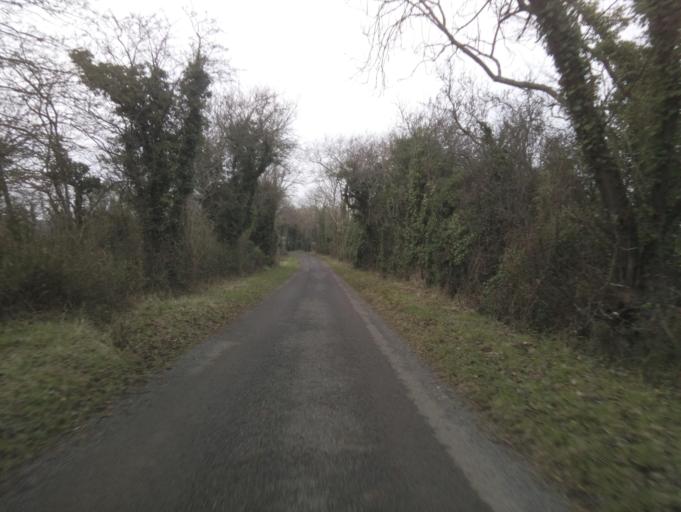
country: GB
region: England
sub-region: Wiltshire
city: Biddestone
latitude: 51.4608
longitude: -2.2111
